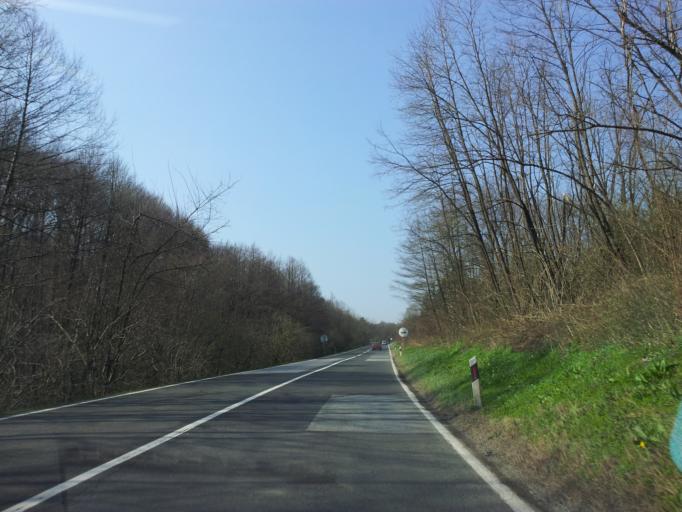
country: HR
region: Karlovacka
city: Vojnic
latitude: 45.2816
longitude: 15.5731
